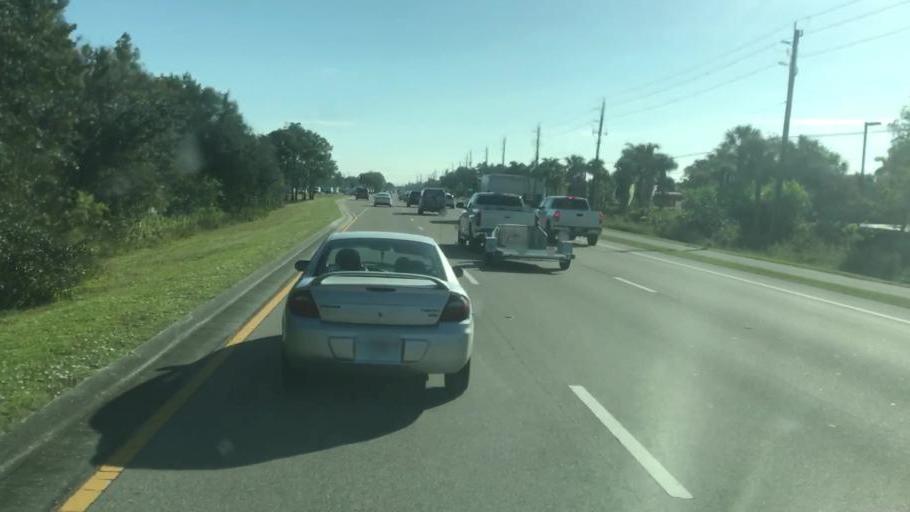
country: US
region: Florida
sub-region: Lee County
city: Villas
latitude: 26.5471
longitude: -81.8104
